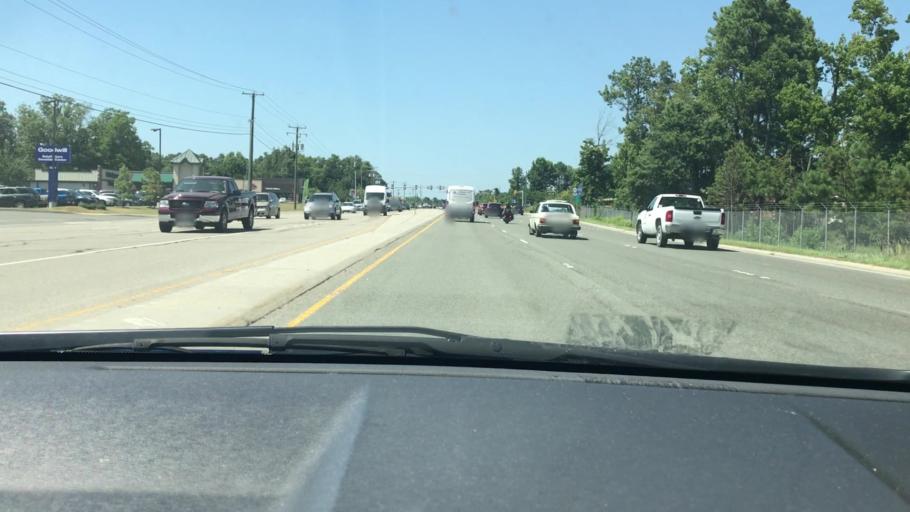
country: US
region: Virginia
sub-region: Henrico County
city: Glen Allen
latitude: 37.6843
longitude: -77.4620
